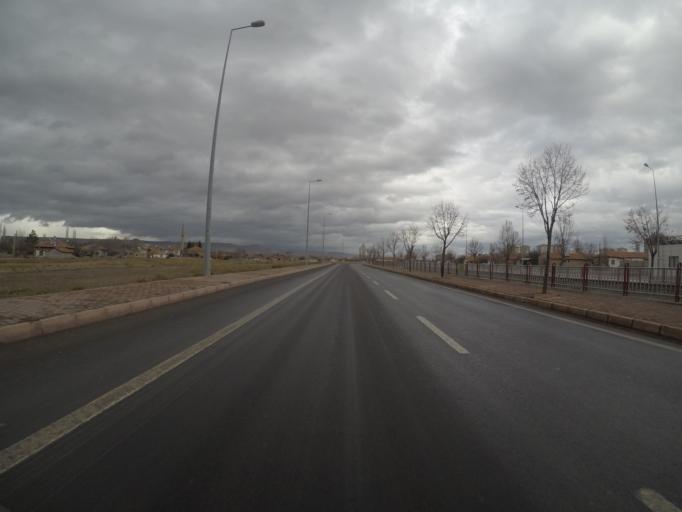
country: TR
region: Kayseri
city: Kayseri
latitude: 38.7535
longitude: 35.4767
